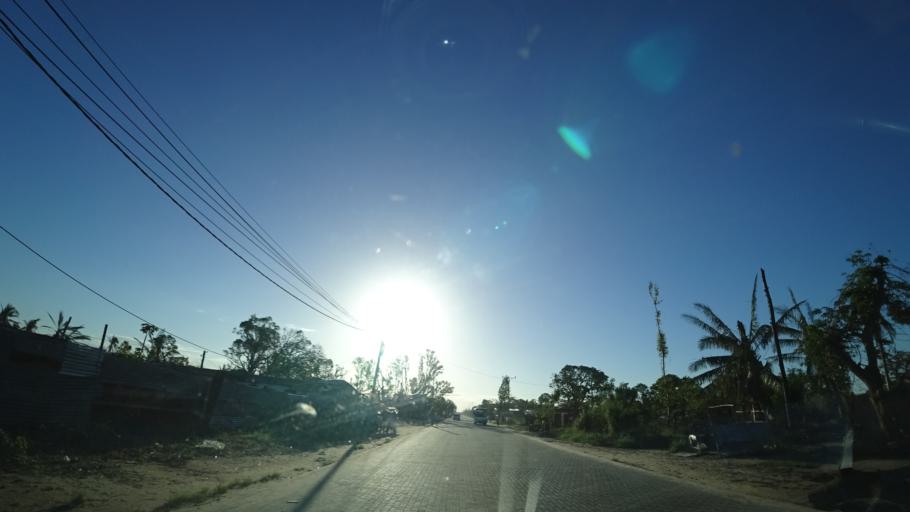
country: MZ
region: Sofala
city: Beira
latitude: -19.7425
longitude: 34.8373
